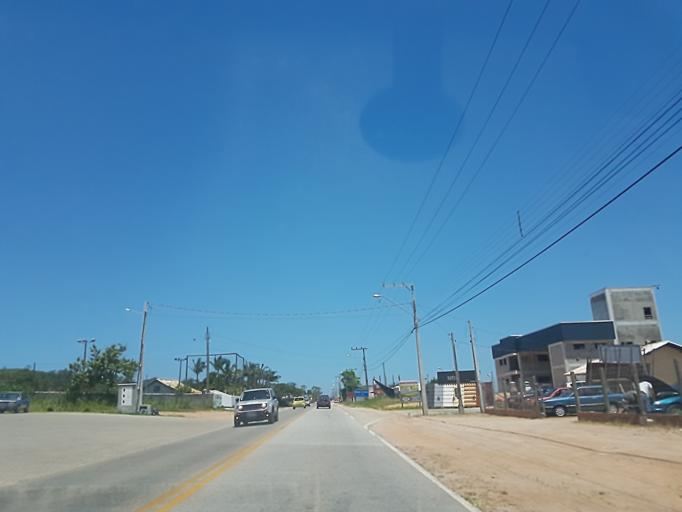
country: BR
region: Santa Catarina
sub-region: Jaguaruna
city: Jaguaruna
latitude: -28.6033
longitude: -49.0362
